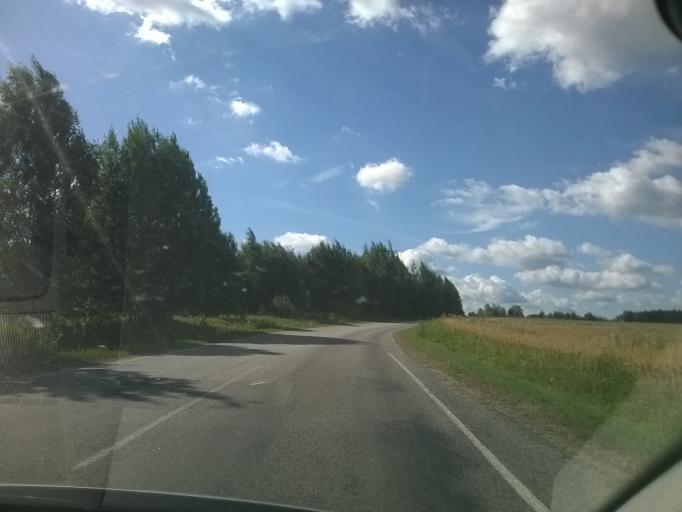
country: EE
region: Vorumaa
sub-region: Voru linn
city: Voru
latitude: 57.7914
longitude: 26.9536
